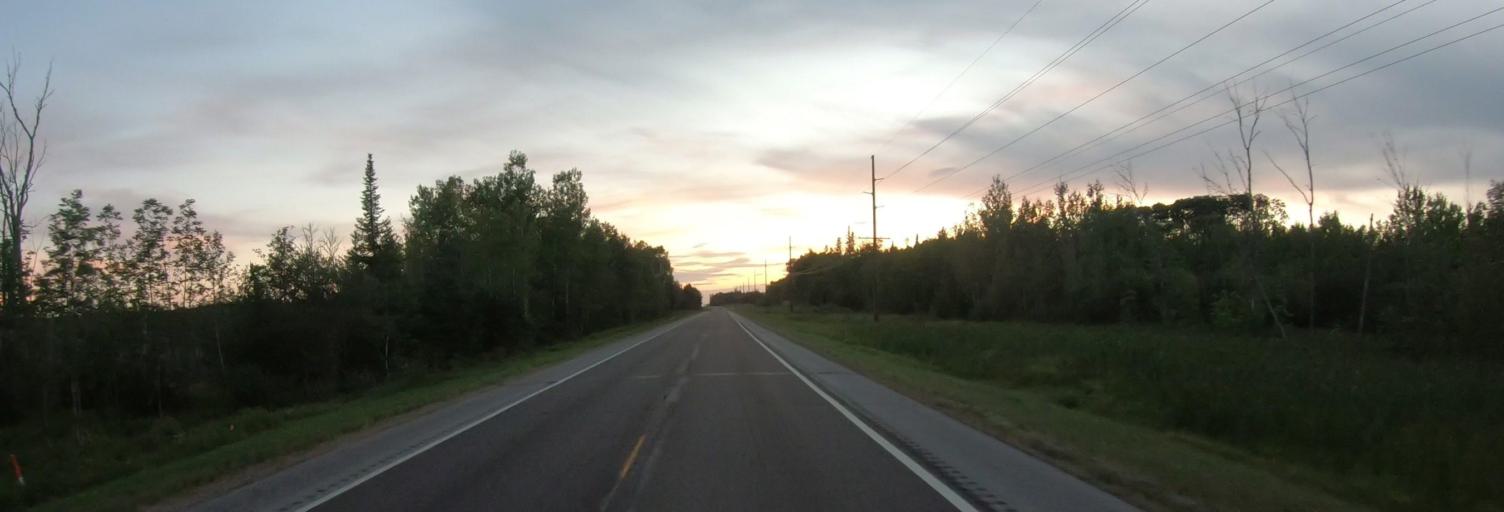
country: US
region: Minnesota
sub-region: Saint Louis County
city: Parkville
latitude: 47.8463
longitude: -92.5397
